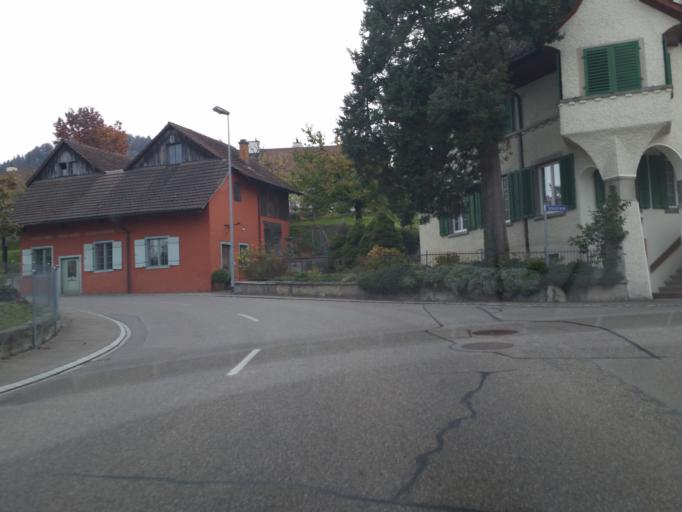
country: CH
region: Zurich
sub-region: Bezirk Buelach
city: Freienstein
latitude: 47.5573
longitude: 8.6052
